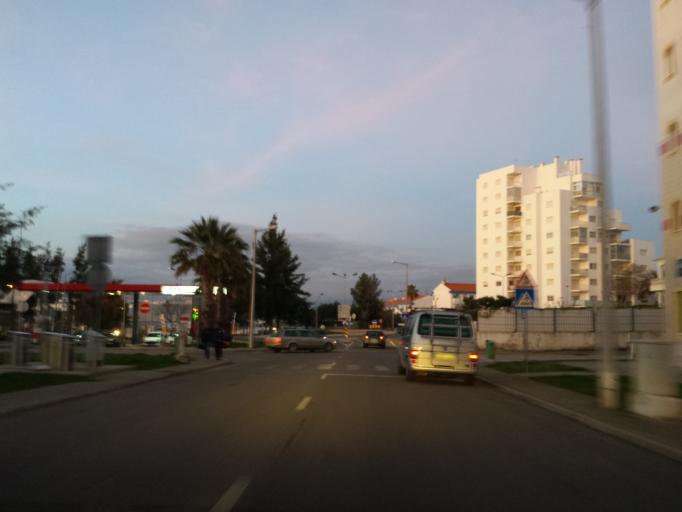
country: PT
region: Faro
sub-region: Lagos
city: Lagos
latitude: 37.0994
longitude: -8.6820
